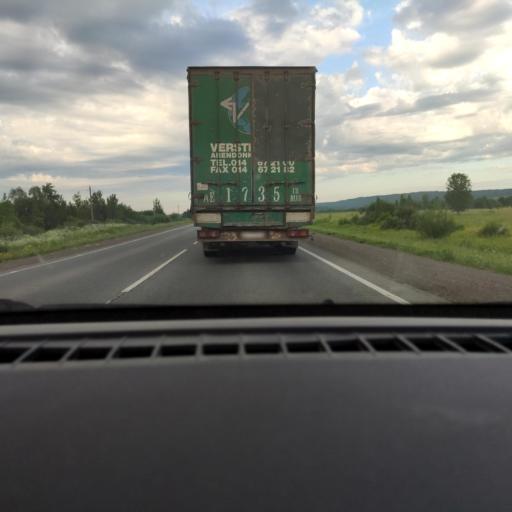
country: RU
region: Udmurtiya
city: Votkinsk
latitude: 57.3526
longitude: 54.4298
